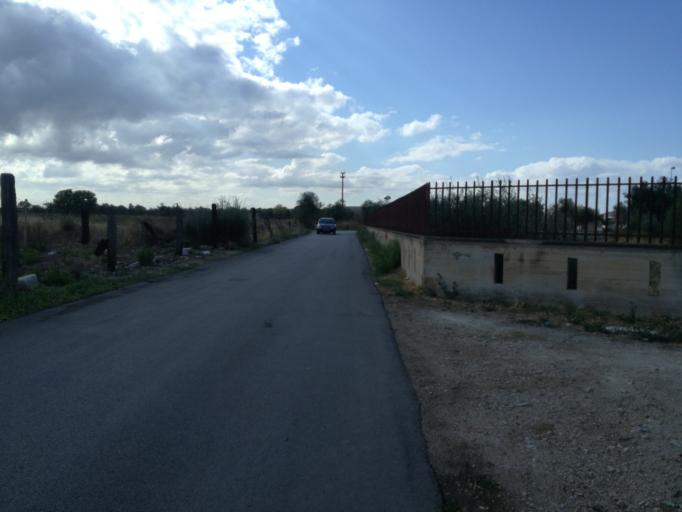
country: IT
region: Apulia
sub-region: Provincia di Bari
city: Triggiano
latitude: 41.0655
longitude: 16.9355
